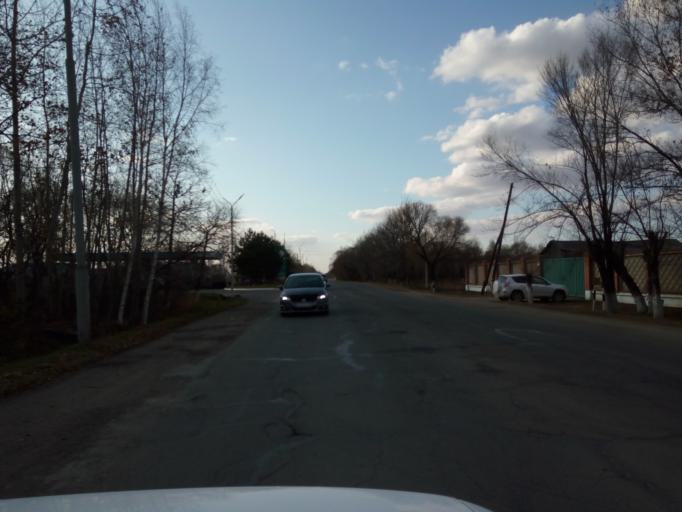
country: RU
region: Primorskiy
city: Dal'nerechensk
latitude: 45.9175
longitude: 133.7630
